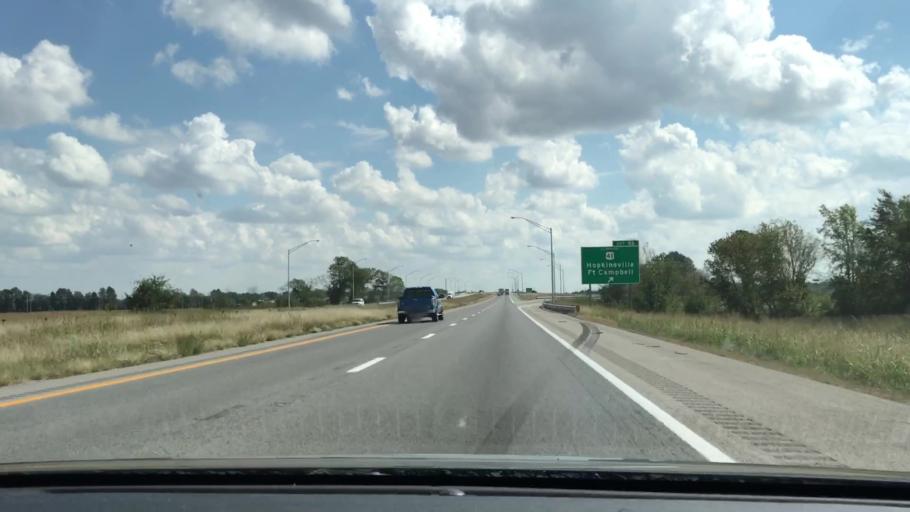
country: US
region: Kentucky
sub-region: Christian County
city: Oak Grove
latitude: 36.7056
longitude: -87.4627
